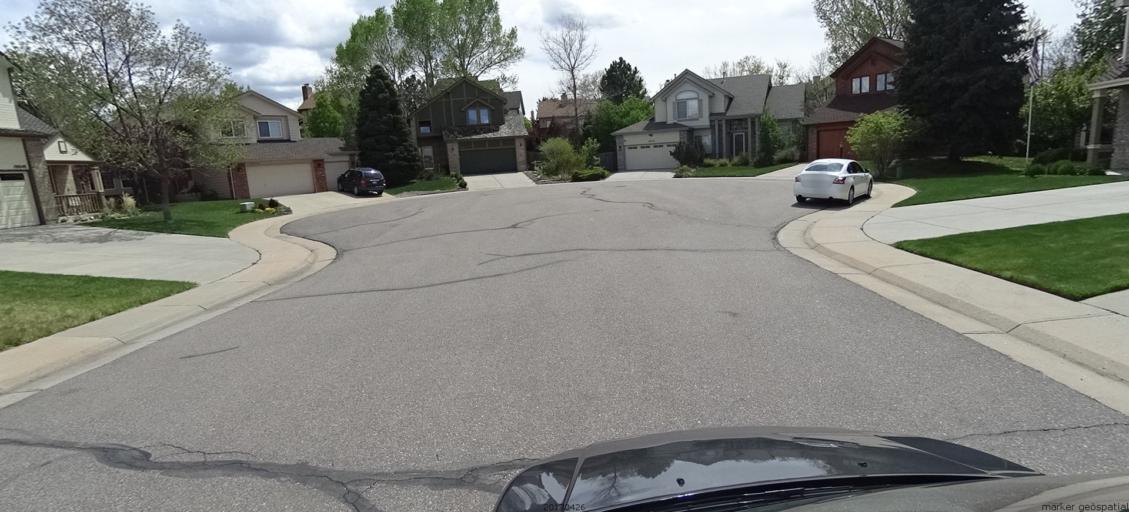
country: US
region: Colorado
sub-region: Douglas County
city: Carriage Club
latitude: 39.5341
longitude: -104.9029
